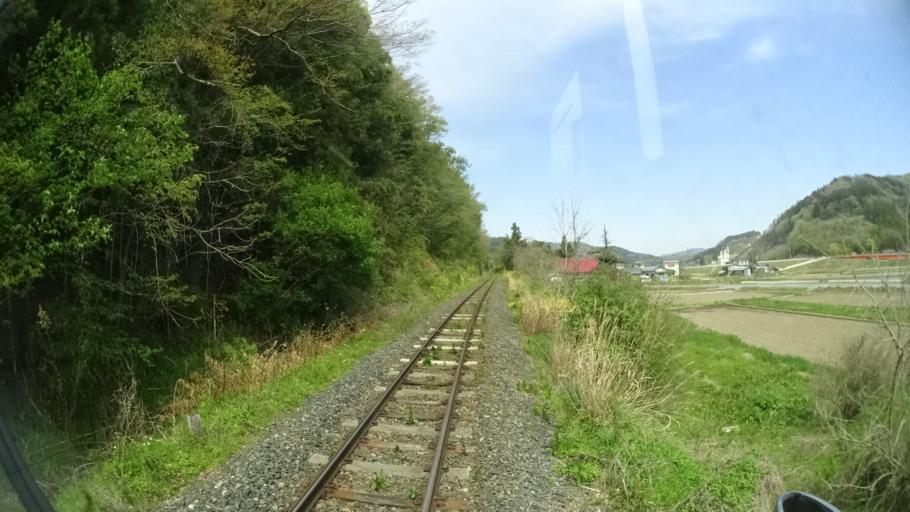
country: JP
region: Iwate
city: Ichinoseki
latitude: 38.9589
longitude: 141.2447
